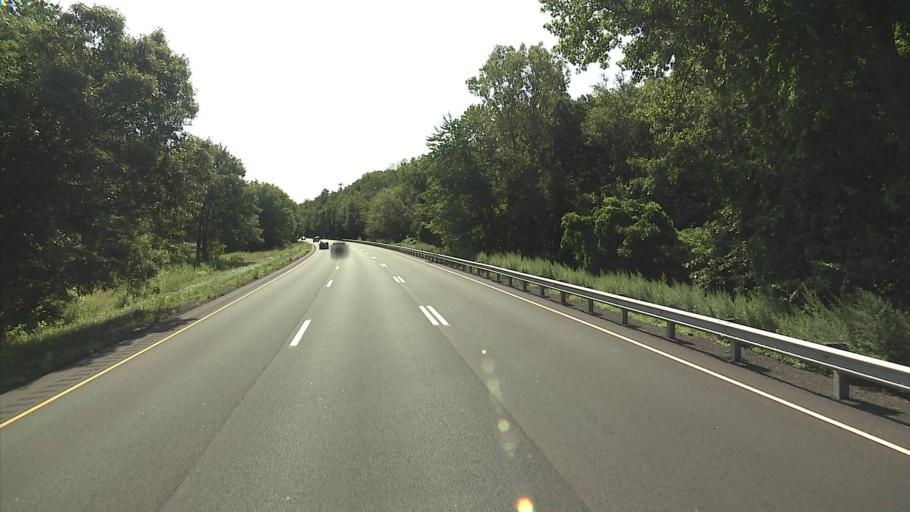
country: US
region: Connecticut
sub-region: Hartford County
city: Glastonbury Center
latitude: 41.7011
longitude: -72.5675
